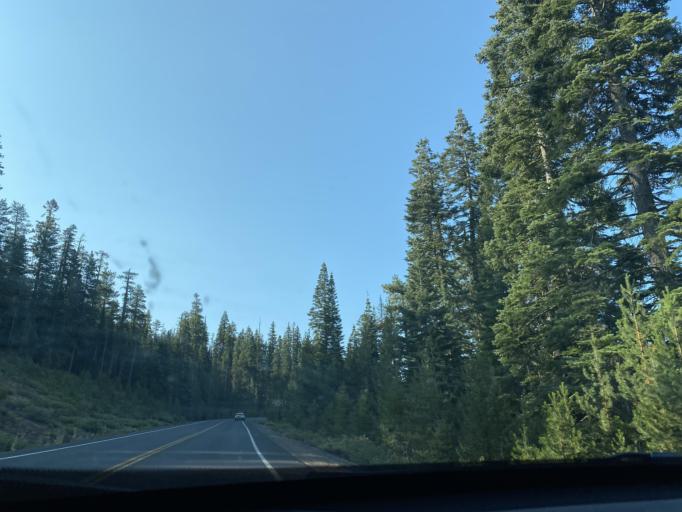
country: US
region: Oregon
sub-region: Deschutes County
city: Three Rivers
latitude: 43.7066
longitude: -121.3170
